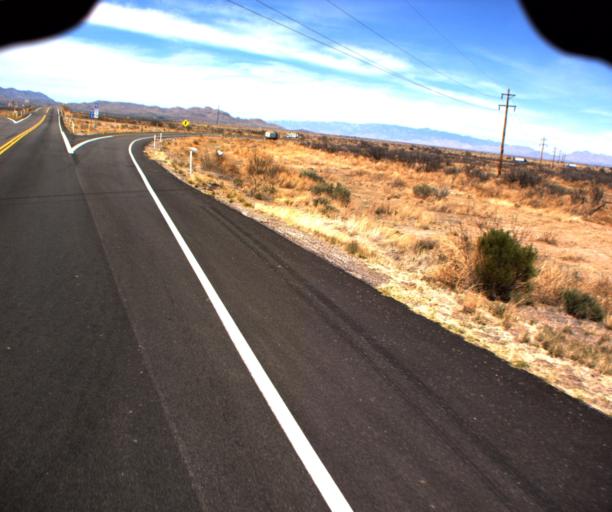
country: US
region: Arizona
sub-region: Cochise County
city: Willcox
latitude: 32.1729
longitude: -109.9476
